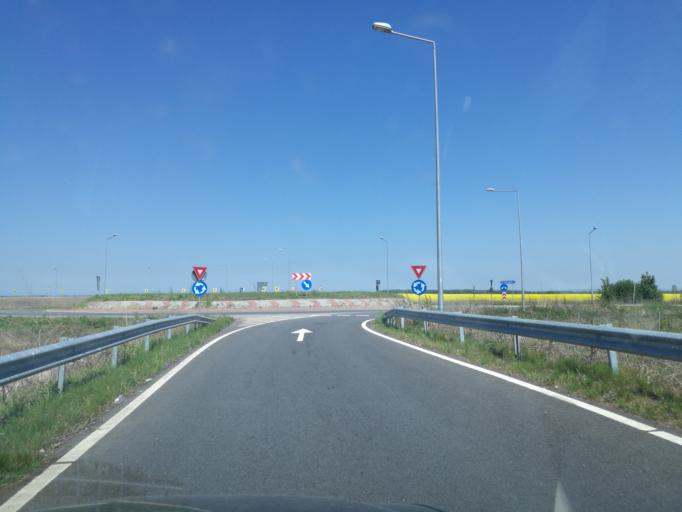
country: RO
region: Prahova
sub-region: Comuna Gherghita
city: Gherghita
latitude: 44.7781
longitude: 26.2535
